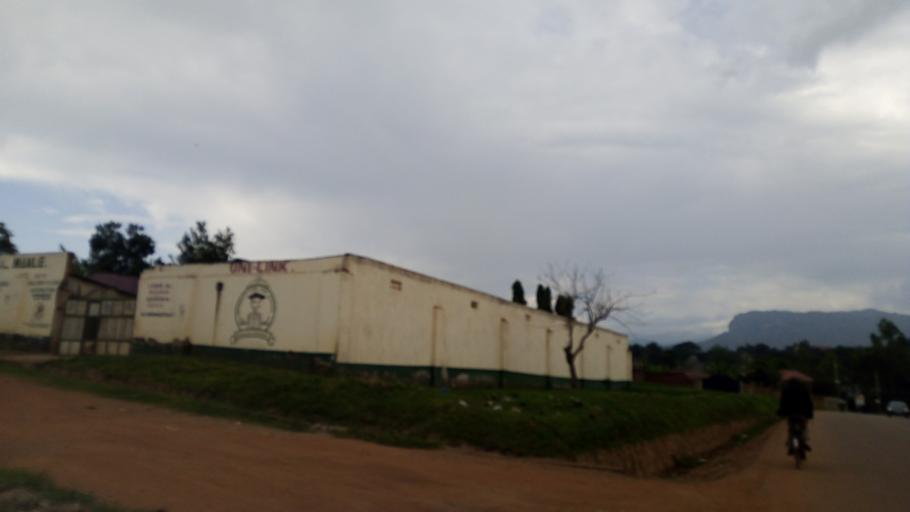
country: UG
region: Eastern Region
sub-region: Mbale District
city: Mbale
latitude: 1.0753
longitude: 34.1679
